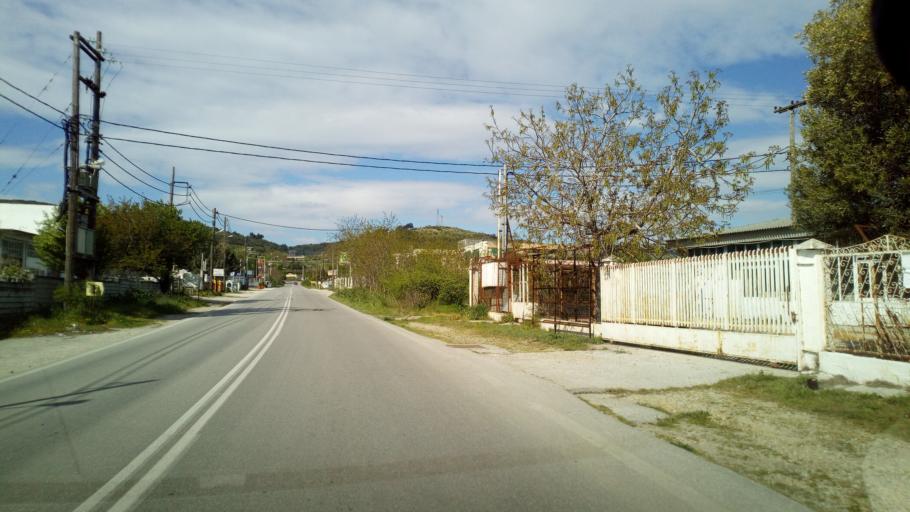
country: GR
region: Central Macedonia
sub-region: Nomos Thessalonikis
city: Lagyna
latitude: 40.7314
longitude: 23.0019
